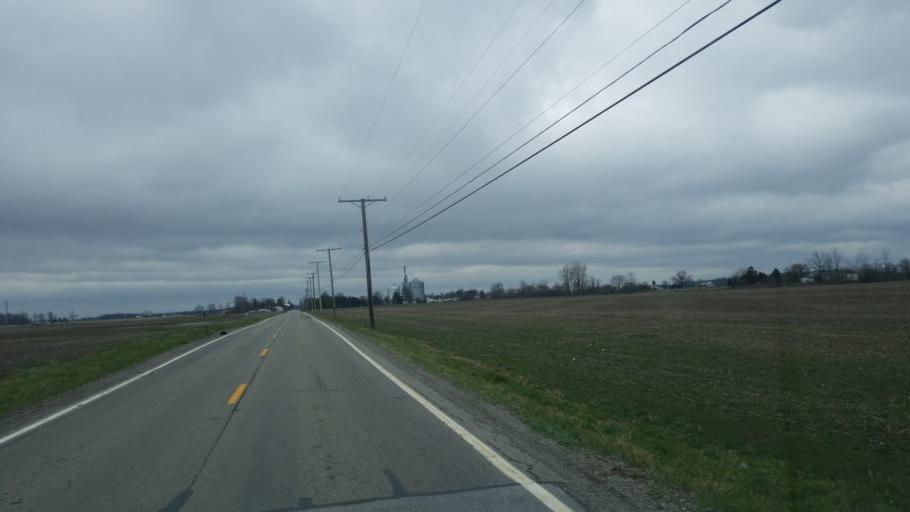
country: US
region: Ohio
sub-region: Hardin County
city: Kenton
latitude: 40.7190
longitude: -83.5616
